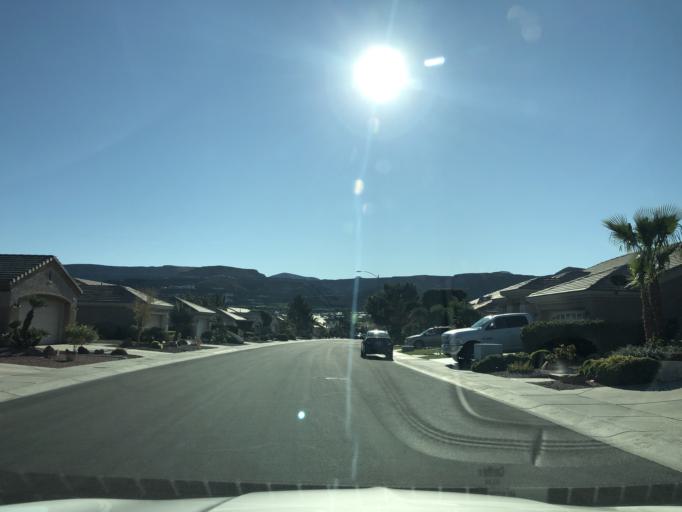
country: US
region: Nevada
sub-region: Clark County
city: Whitney
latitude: 36.0074
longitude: -115.0737
